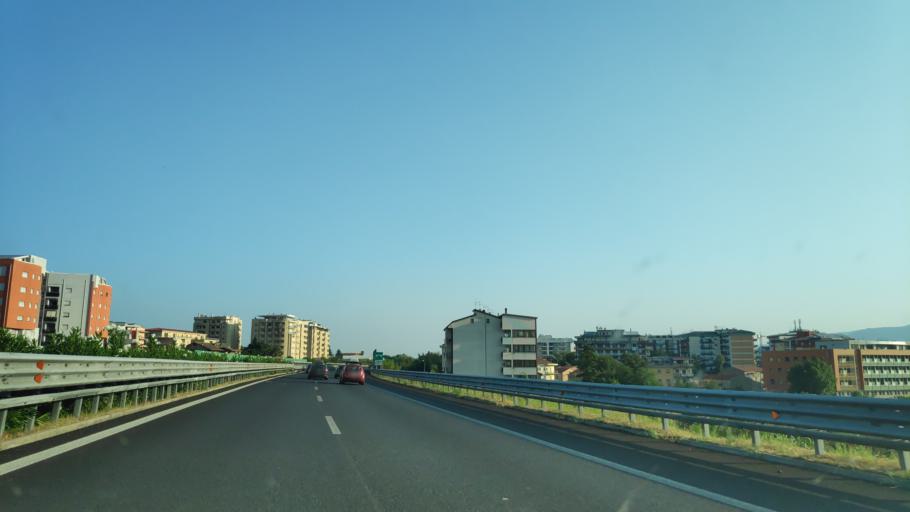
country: IT
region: Calabria
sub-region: Provincia di Cosenza
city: Cosenza
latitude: 39.3209
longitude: 16.2404
